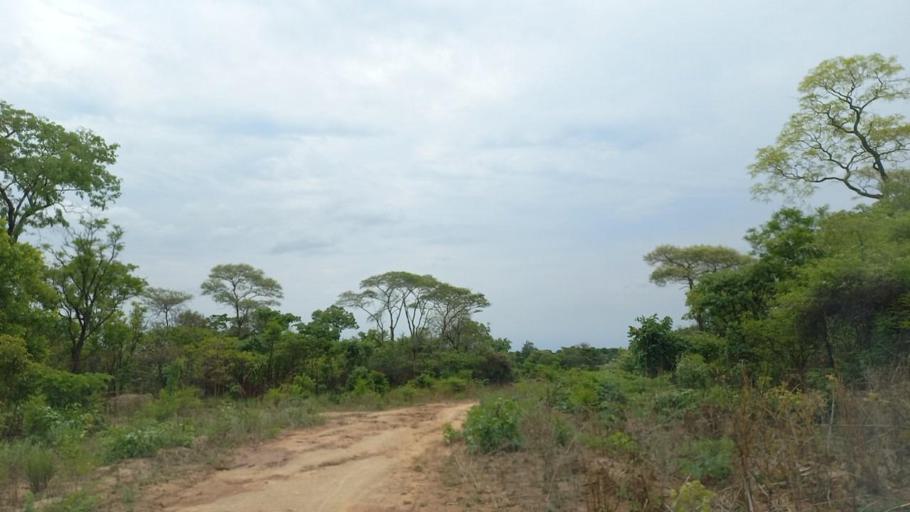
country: ZM
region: North-Western
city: Kalengwa
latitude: -13.6350
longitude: 24.9797
